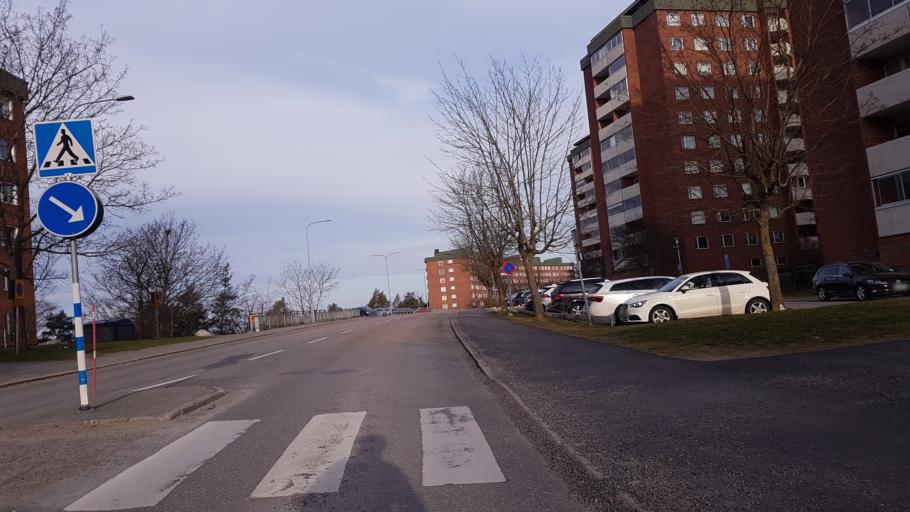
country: SE
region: Stockholm
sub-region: Lidingo
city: Lidingoe
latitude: 59.3467
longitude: 18.1443
